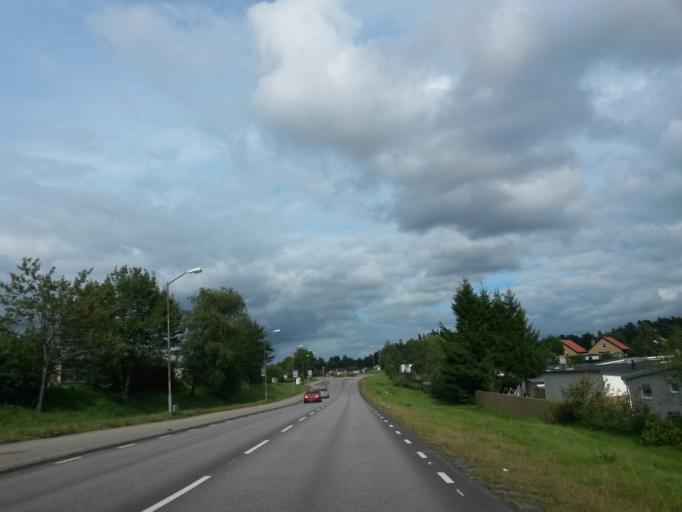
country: SE
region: Vaestra Goetaland
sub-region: Boras Kommun
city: Boras
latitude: 57.7151
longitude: 12.9751
